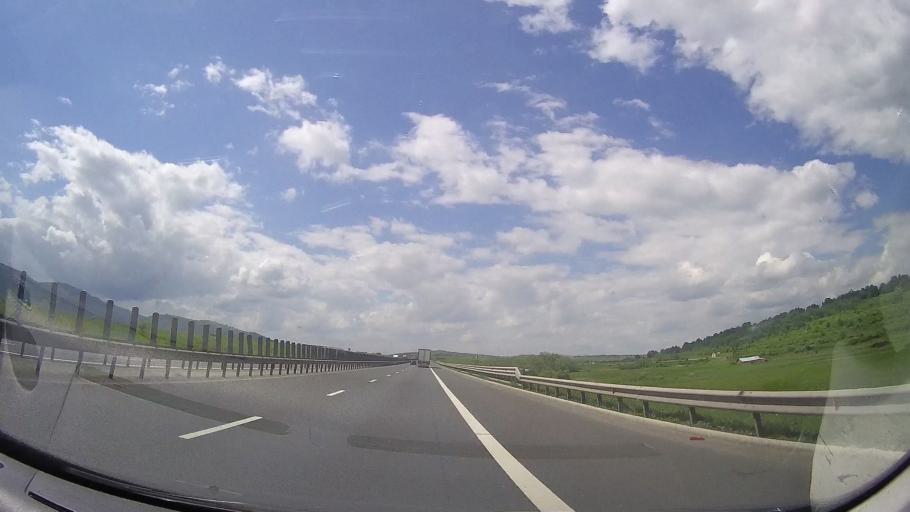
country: RO
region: Sibiu
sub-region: Oras Saliste
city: Saliste
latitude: 45.7983
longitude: 23.9295
